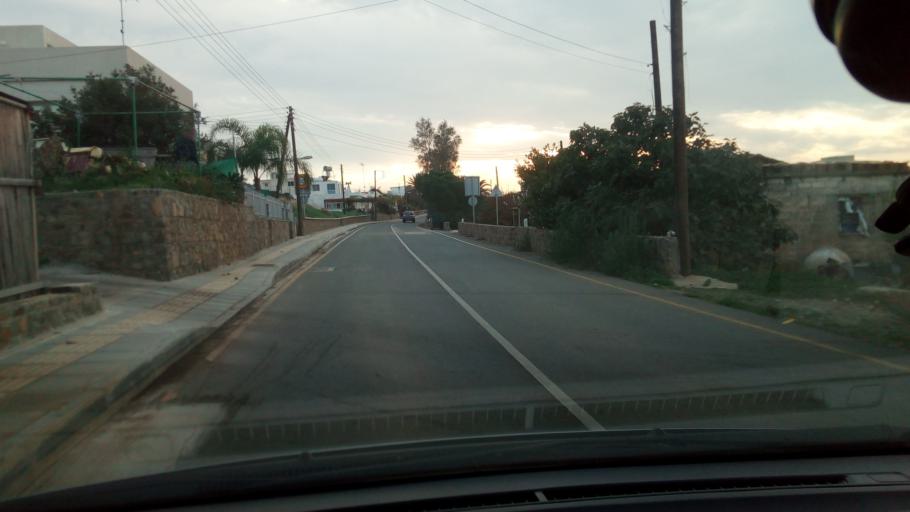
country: CY
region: Lefkosia
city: Kato Pyrgos
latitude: 35.1596
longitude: 32.5445
